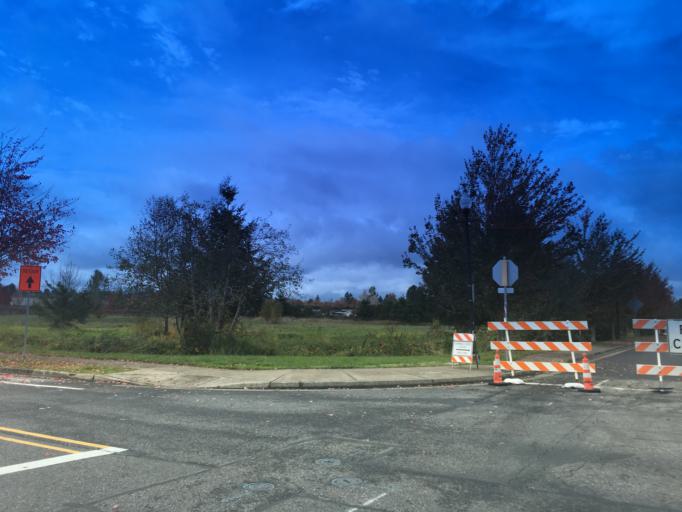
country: US
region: Oregon
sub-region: Multnomah County
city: Fairview
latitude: 45.5343
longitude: -122.4276
